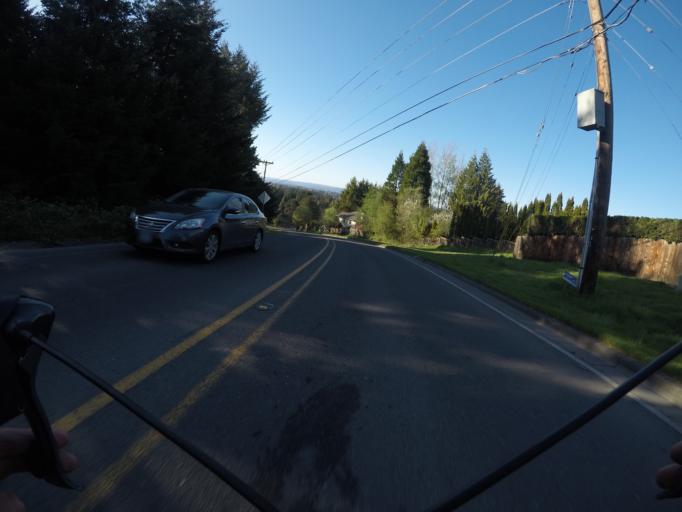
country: US
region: Oregon
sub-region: Washington County
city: Aloha
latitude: 45.4650
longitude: -122.8666
